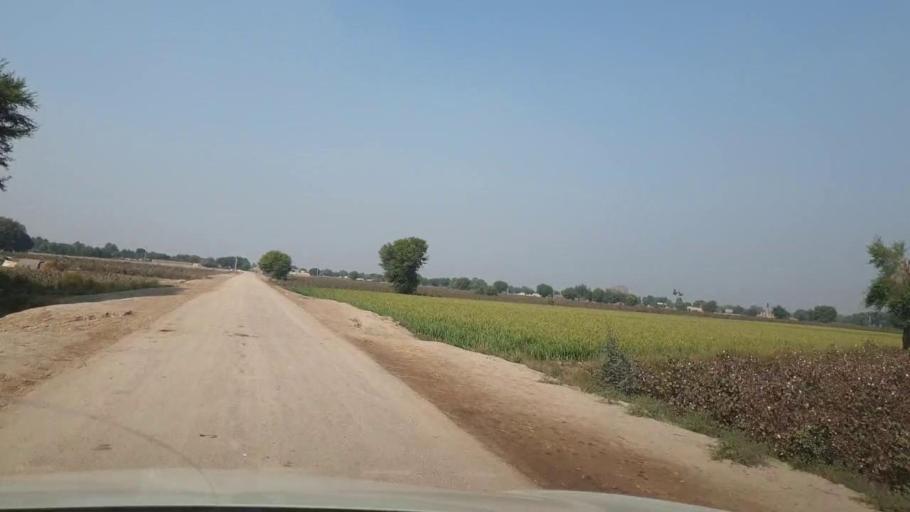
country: PK
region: Sindh
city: Bhan
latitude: 26.5418
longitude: 67.7406
